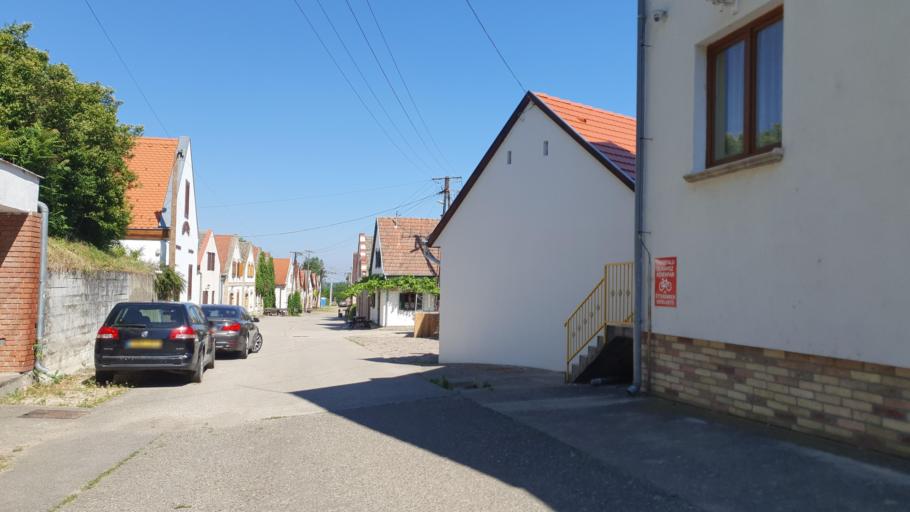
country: HU
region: Bacs-Kiskun
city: Hajos
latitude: 46.3851
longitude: 19.1501
